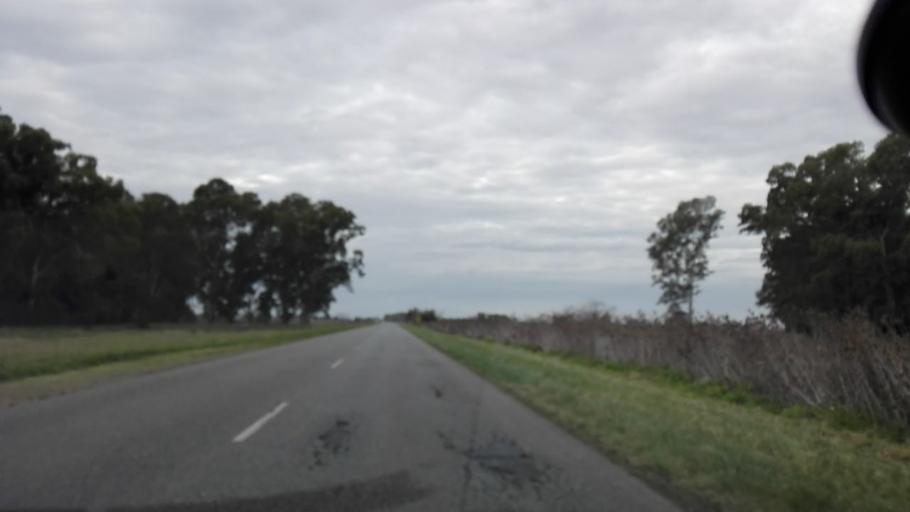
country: AR
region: Buenos Aires
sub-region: Partido de Rauch
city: Rauch
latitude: -36.4211
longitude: -59.0003
